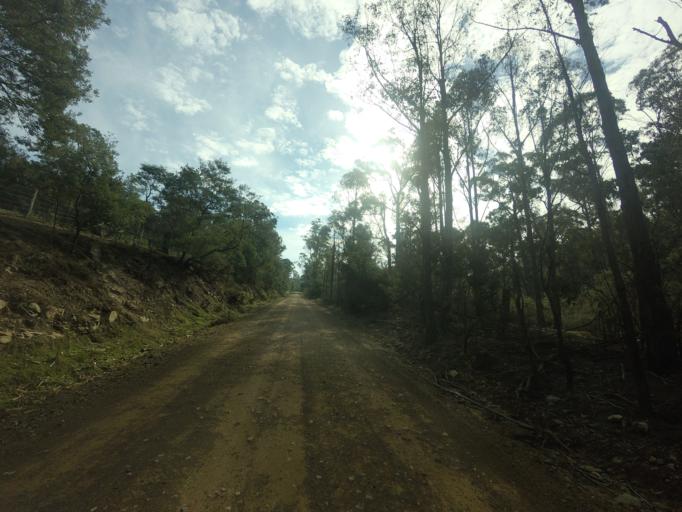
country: AU
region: Tasmania
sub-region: Sorell
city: Sorell
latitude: -42.5635
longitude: 147.4676
